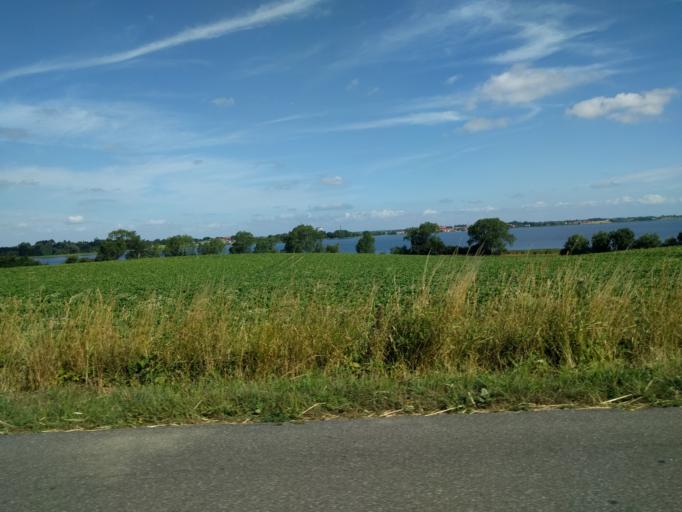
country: DK
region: Zealand
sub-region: Vordingborg Kommune
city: Stege
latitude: 54.9621
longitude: 12.2850
